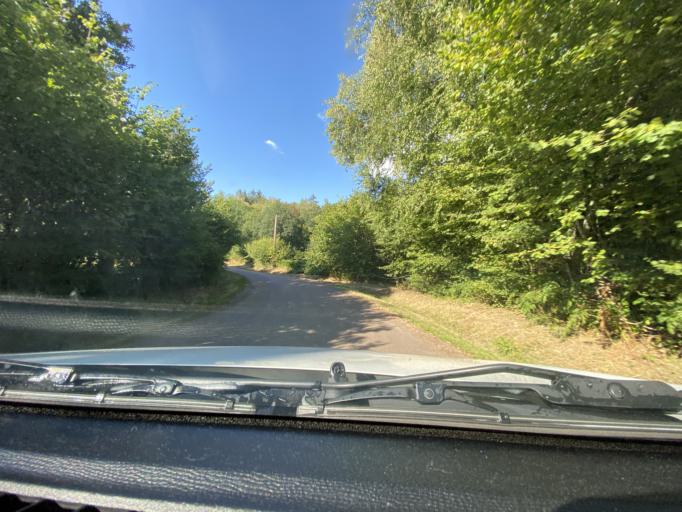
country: FR
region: Bourgogne
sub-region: Departement de la Cote-d'Or
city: Saulieu
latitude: 47.2923
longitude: 4.1709
